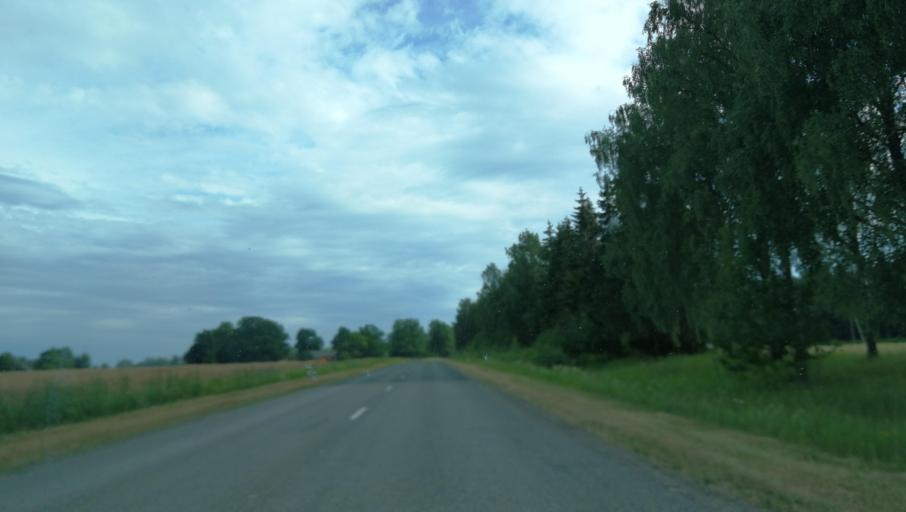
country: LV
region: Valmieras Rajons
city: Valmiera
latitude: 57.5973
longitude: 25.4597
